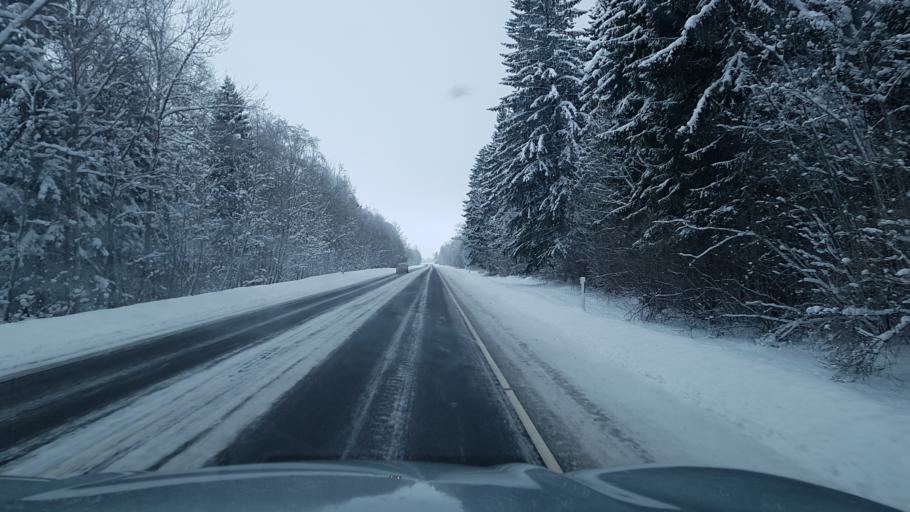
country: EE
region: Ida-Virumaa
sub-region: Johvi vald
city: Johvi
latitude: 59.2798
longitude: 27.3927
